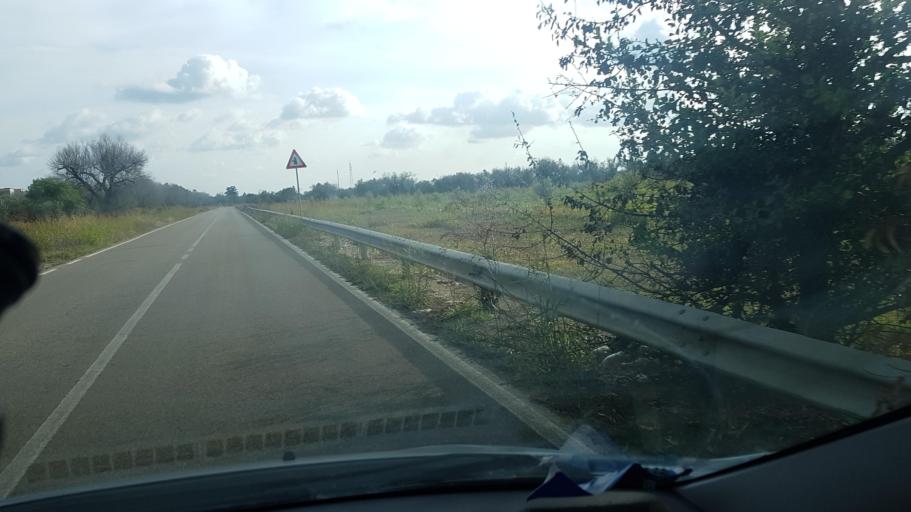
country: IT
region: Apulia
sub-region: Provincia di Brindisi
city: Cellino San Marco
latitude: 40.4527
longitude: 17.9552
